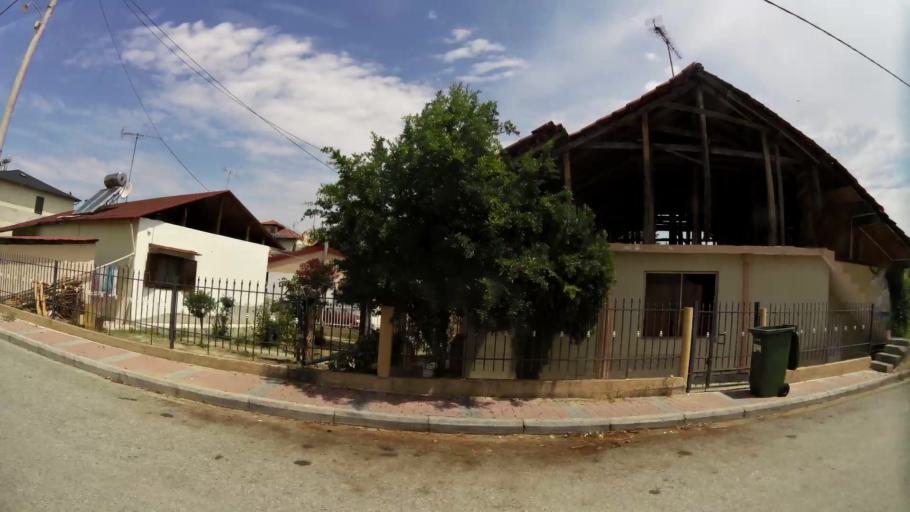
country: GR
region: Central Macedonia
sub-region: Nomos Pierias
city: Katerini
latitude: 40.2606
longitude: 22.5008
